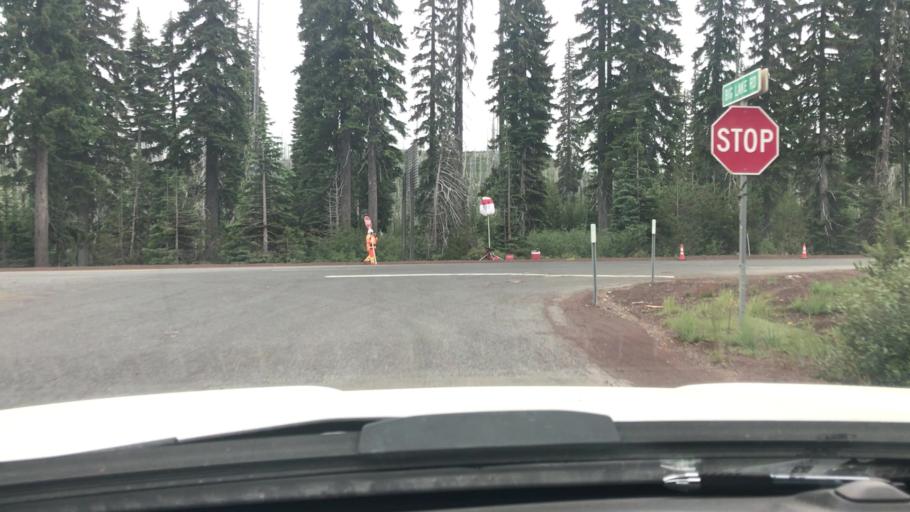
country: US
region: Oregon
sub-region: Deschutes County
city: Sisters
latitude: 44.4213
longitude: -121.8618
